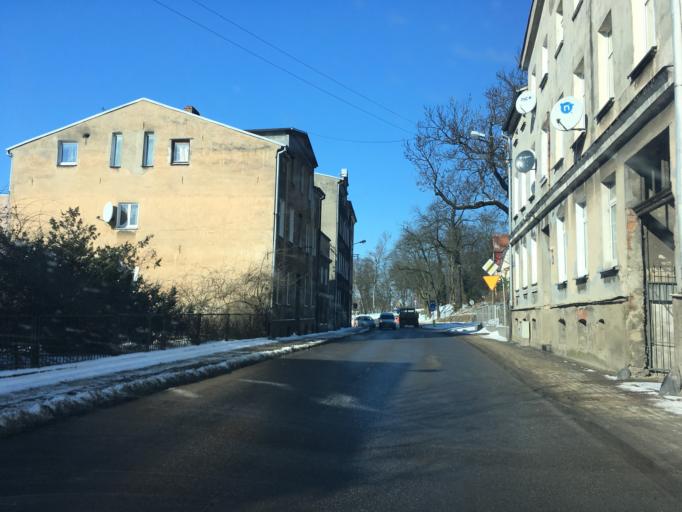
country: PL
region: Pomeranian Voivodeship
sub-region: Slupsk
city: Slupsk
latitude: 54.4682
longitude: 17.0422
